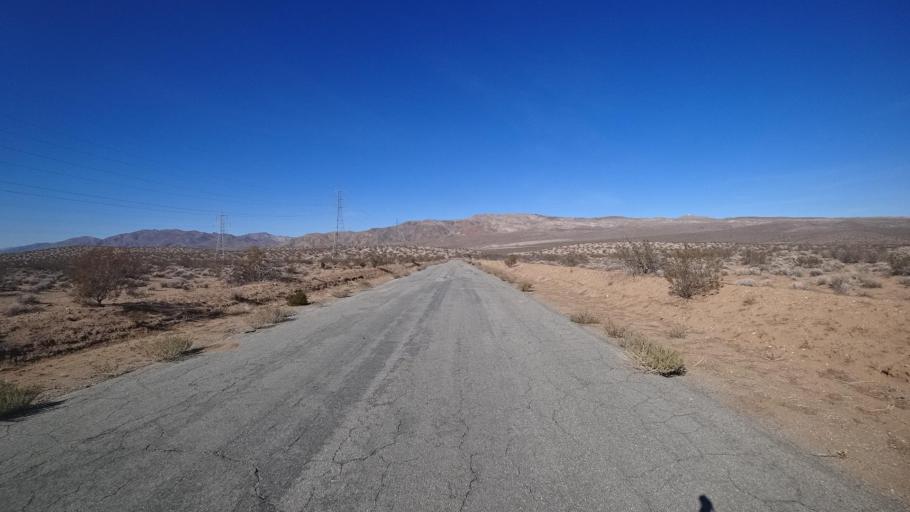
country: US
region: California
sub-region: Kern County
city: Ridgecrest
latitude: 35.4102
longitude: -117.6841
